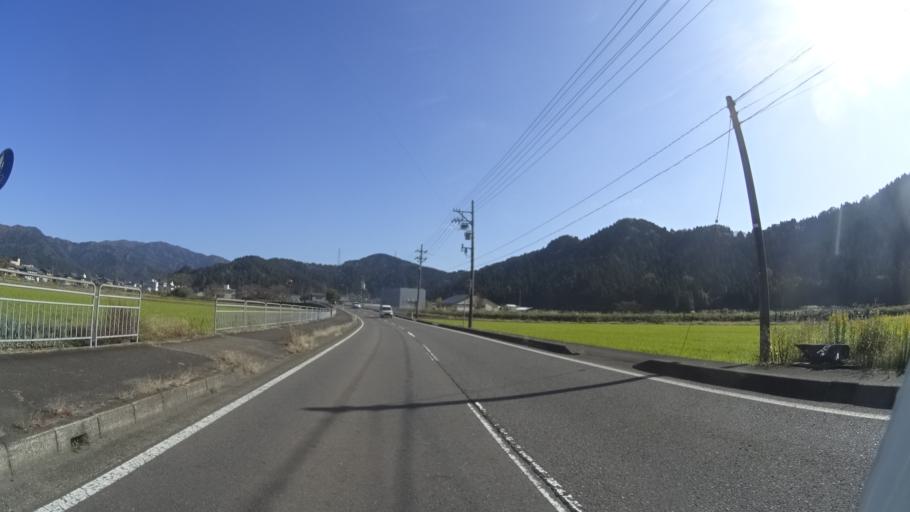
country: JP
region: Fukui
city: Sabae
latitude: 35.9465
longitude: 136.2651
